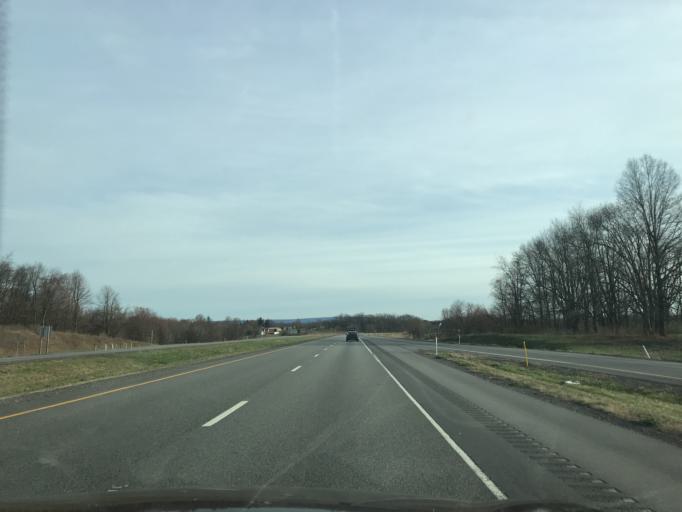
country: US
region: Pennsylvania
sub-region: Northumberland County
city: Watsontown
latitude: 41.1201
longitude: -76.8016
